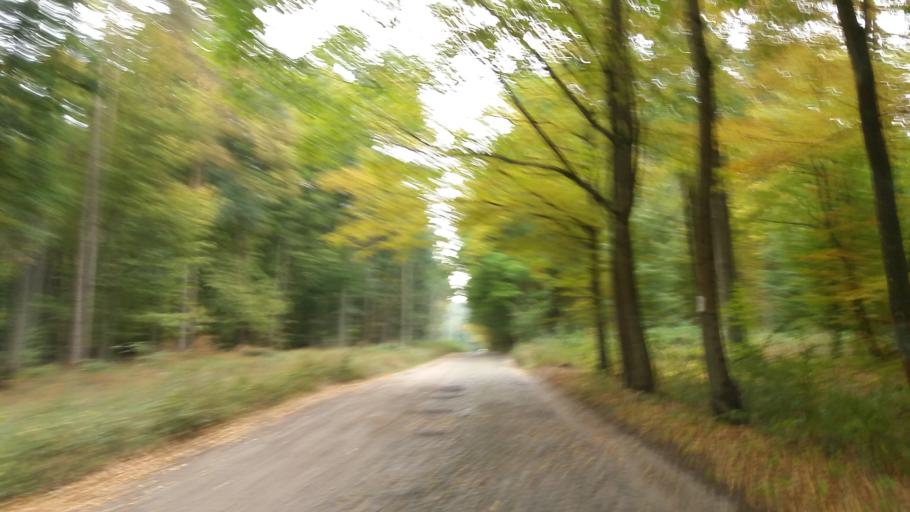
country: PL
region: West Pomeranian Voivodeship
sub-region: Powiat mysliborski
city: Barlinek
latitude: 52.9455
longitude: 15.2500
